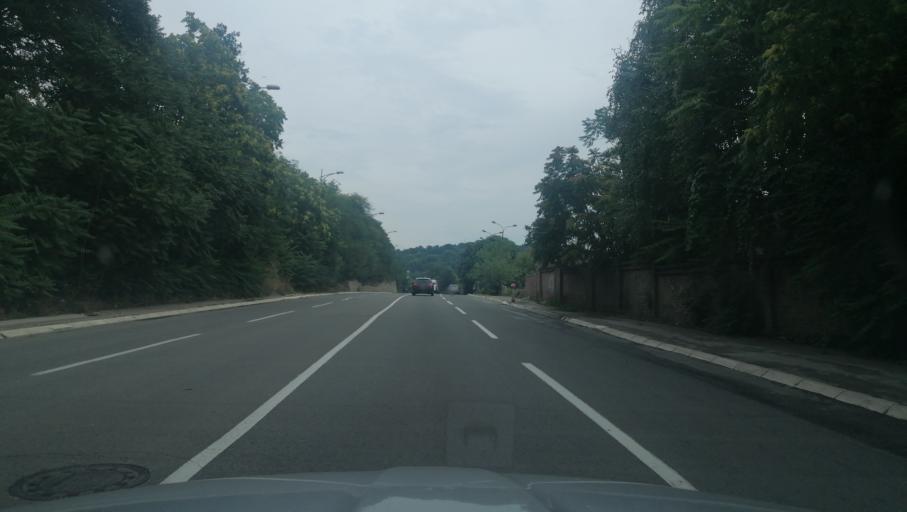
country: RS
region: Central Serbia
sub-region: Belgrade
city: Rakovica
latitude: 44.7375
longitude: 20.4404
